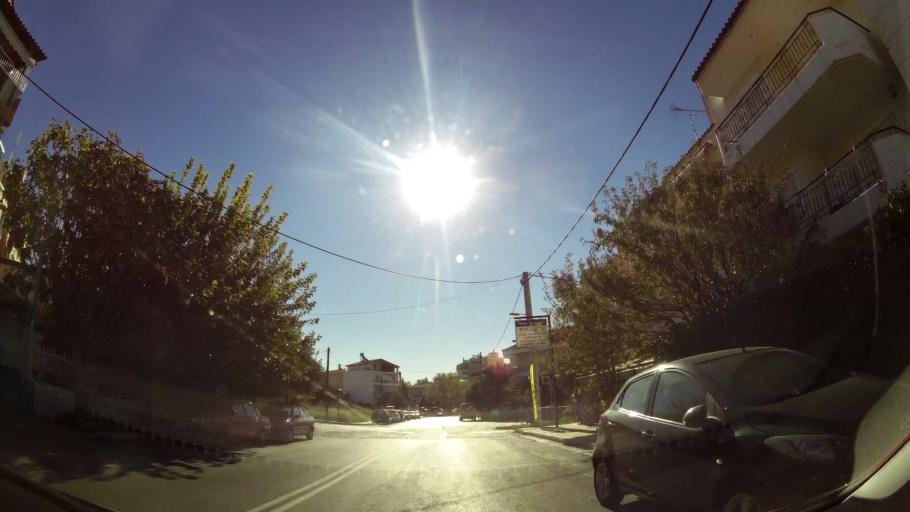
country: GR
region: Attica
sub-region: Nomarchia Anatolikis Attikis
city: Gerakas
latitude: 38.0133
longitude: 23.8567
